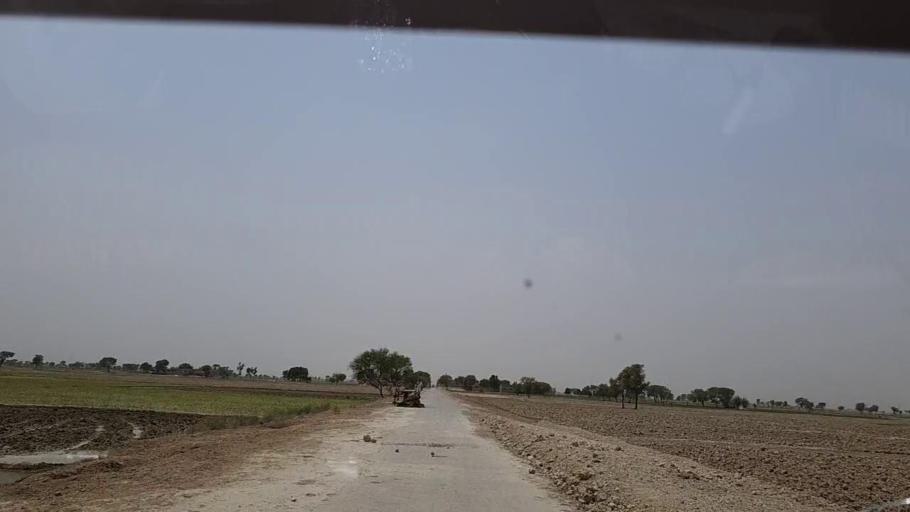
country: PK
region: Sindh
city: Khairpur Nathan Shah
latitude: 27.0059
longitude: 67.6360
